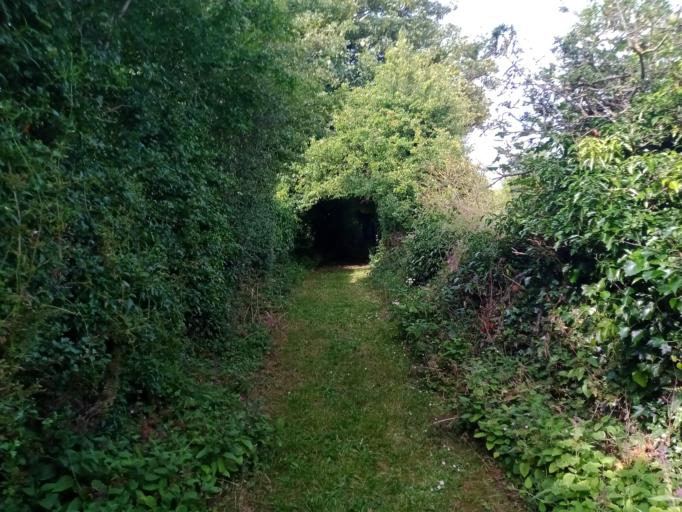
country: IE
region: Leinster
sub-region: Laois
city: Rathdowney
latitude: 52.8155
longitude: -7.4753
